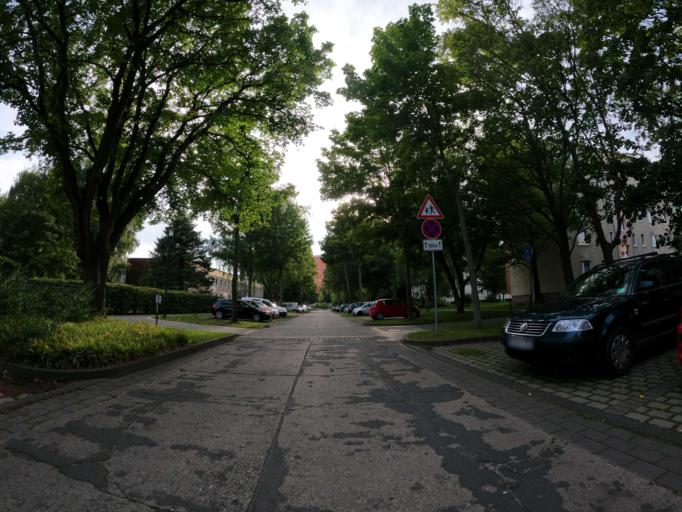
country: DE
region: Mecklenburg-Vorpommern
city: Kramerhof
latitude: 54.3303
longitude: 13.0564
